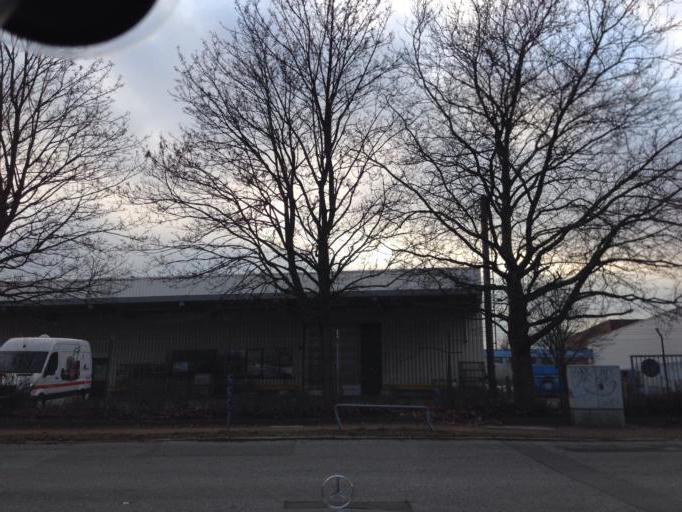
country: DE
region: Hamburg
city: Wandsbek
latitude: 53.5773
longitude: 10.1106
